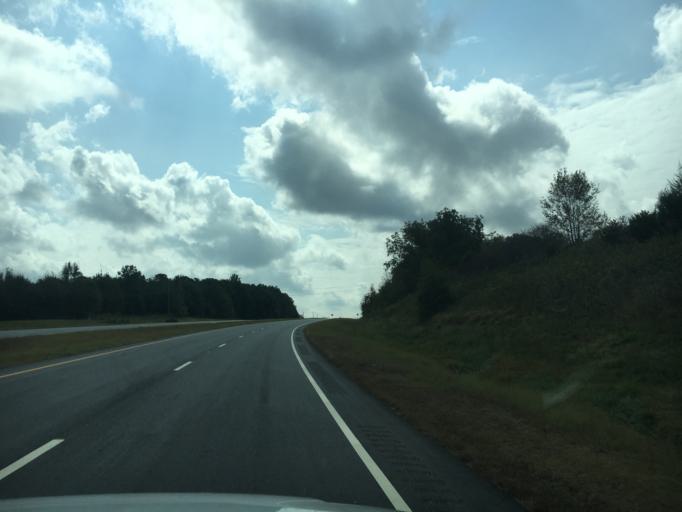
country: US
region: Georgia
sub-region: Hart County
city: Royston
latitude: 34.2933
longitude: -83.0971
